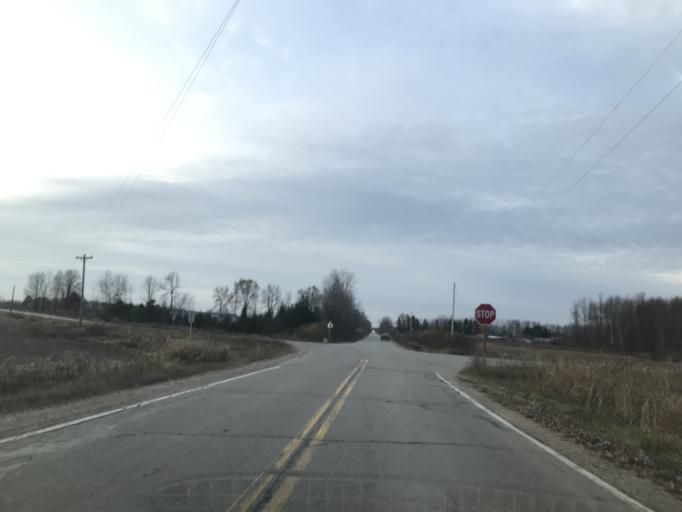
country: US
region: Wisconsin
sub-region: Marinette County
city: Peshtigo
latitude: 45.0940
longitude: -87.7994
